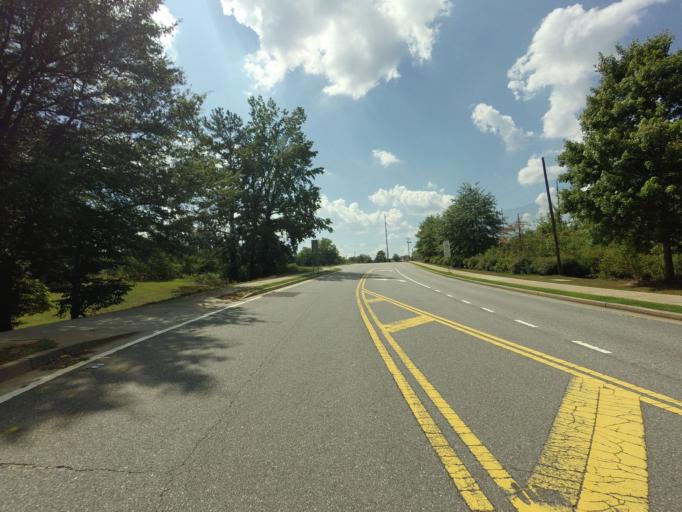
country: US
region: Georgia
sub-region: Fulton County
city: Johns Creek
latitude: 34.0394
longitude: -84.1826
